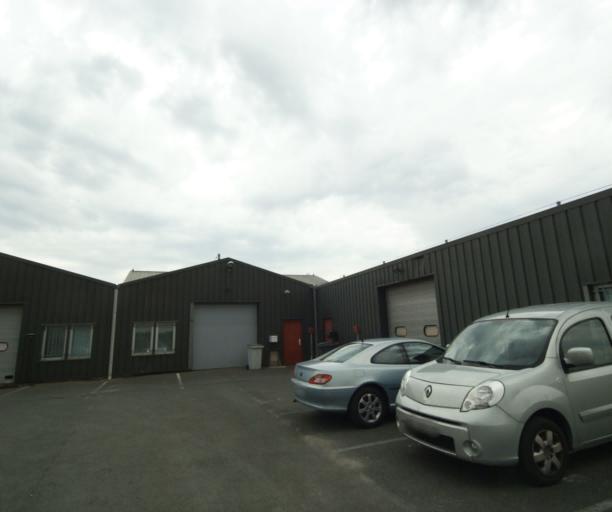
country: FR
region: Poitou-Charentes
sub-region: Departement de la Charente-Maritime
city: Tonnay-Charente
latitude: 45.9529
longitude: -0.8916
